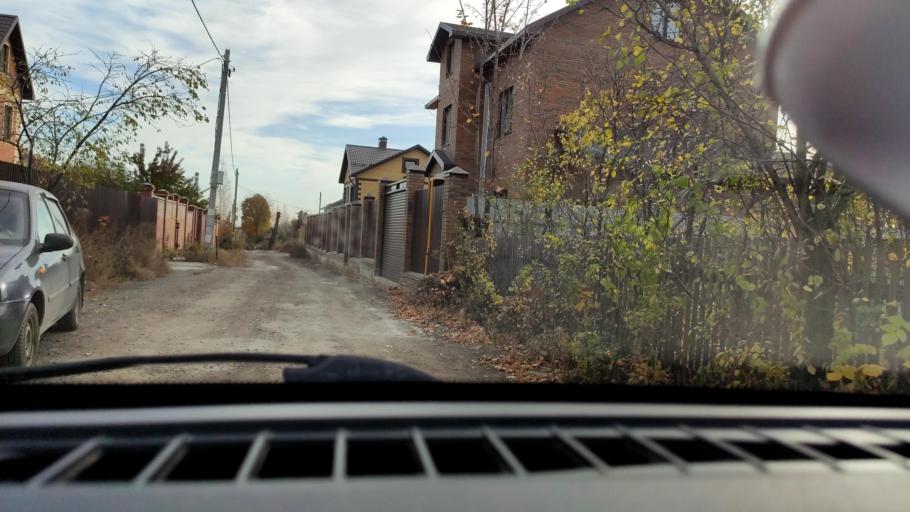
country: RU
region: Samara
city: Petra-Dubrava
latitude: 53.2669
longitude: 50.2643
